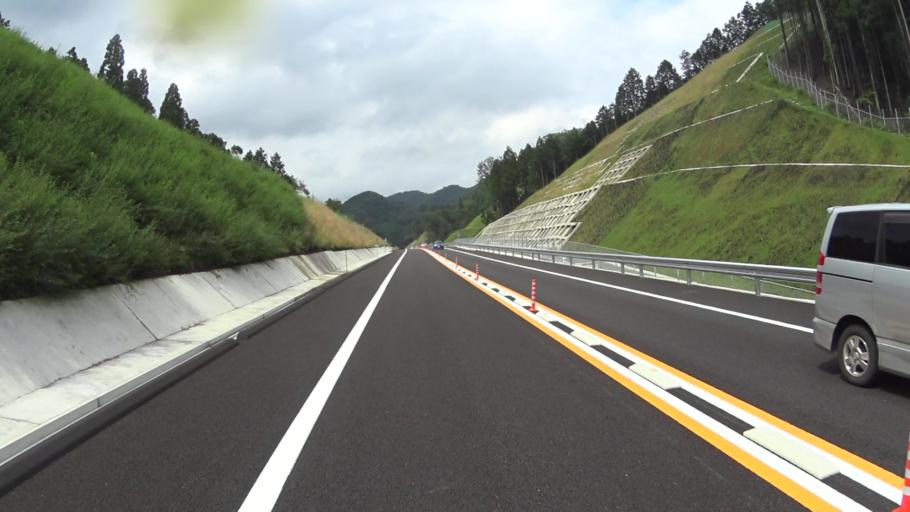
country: JP
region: Kyoto
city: Ayabe
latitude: 35.2217
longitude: 135.3429
